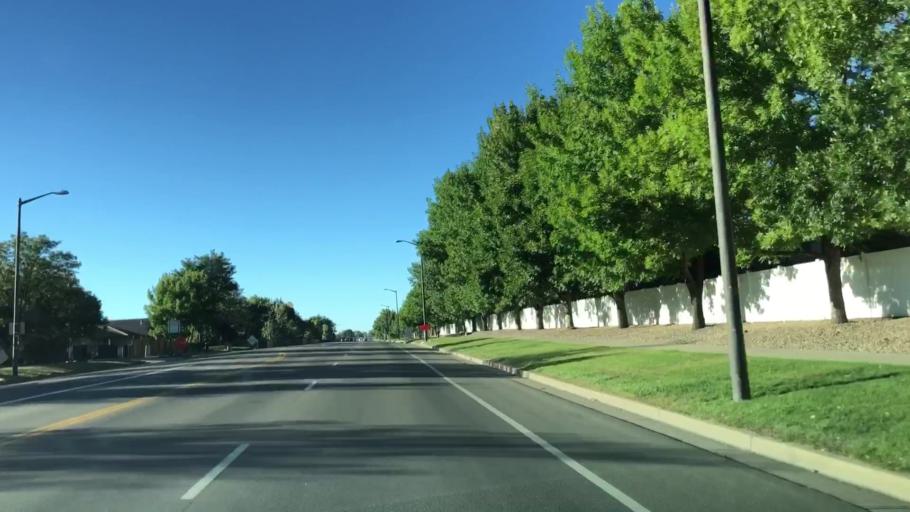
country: US
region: Colorado
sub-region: Larimer County
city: Loveland
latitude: 40.3919
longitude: -105.1160
